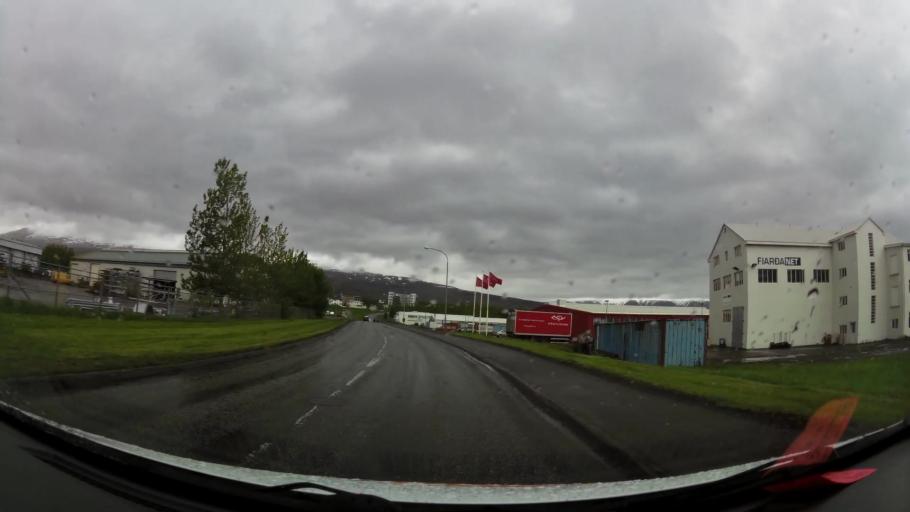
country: IS
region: Northeast
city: Akureyri
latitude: 65.6924
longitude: -18.0969
